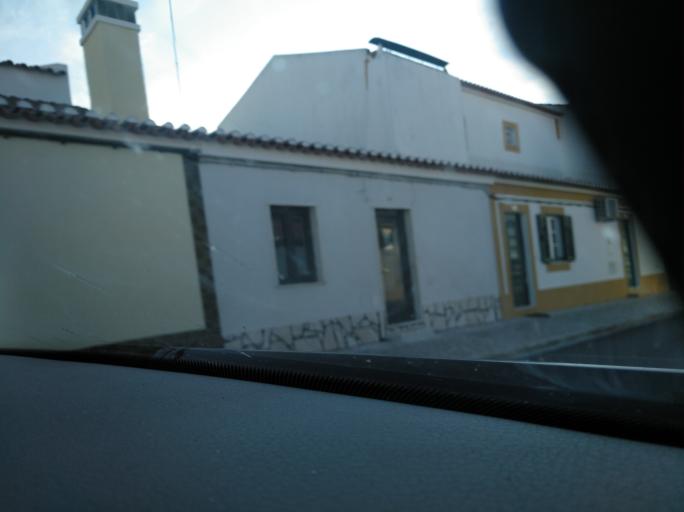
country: PT
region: Evora
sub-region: Estremoz
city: Estremoz
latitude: 38.9525
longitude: -7.5021
